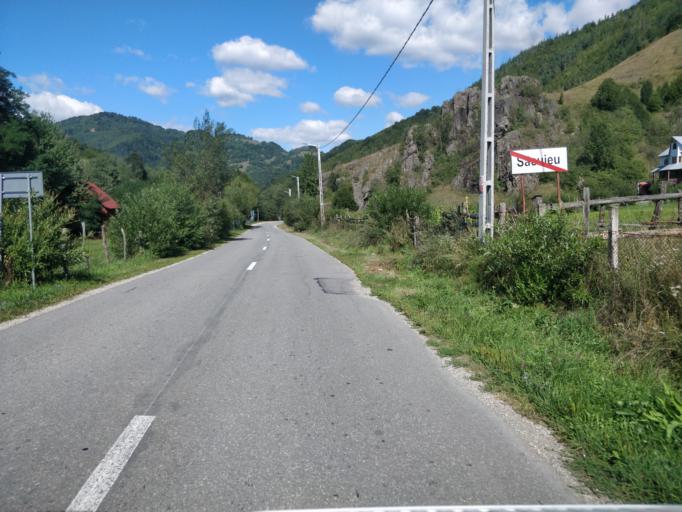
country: RO
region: Cluj
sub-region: Comuna Sacueu
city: Sacuieu
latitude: 46.8280
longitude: 22.8780
